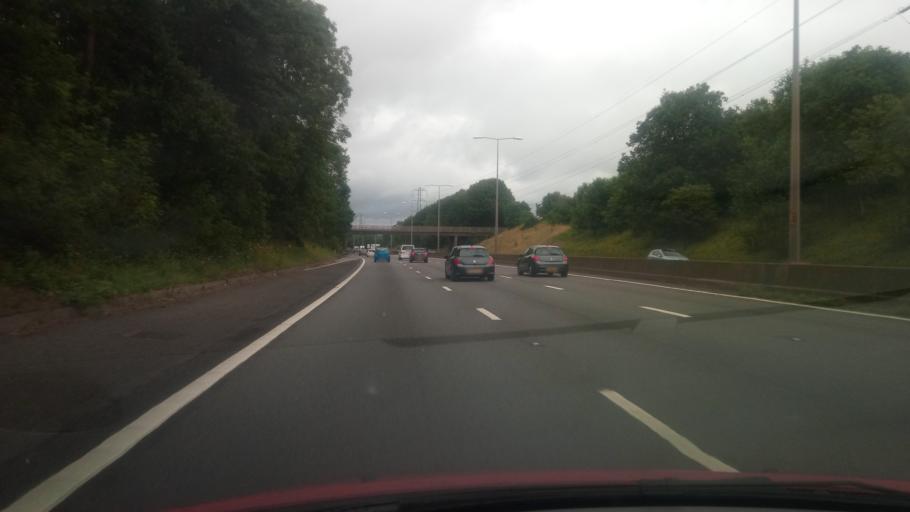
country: GB
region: England
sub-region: City and Borough of Birmingham
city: Bartley Green
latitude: 52.4115
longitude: -2.0279
